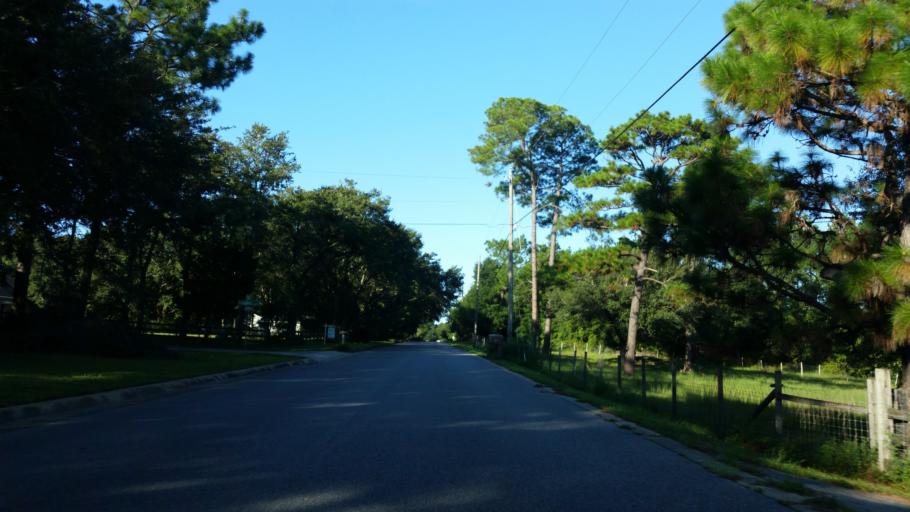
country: US
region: Florida
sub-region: Escambia County
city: Bellview
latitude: 30.4927
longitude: -87.3333
